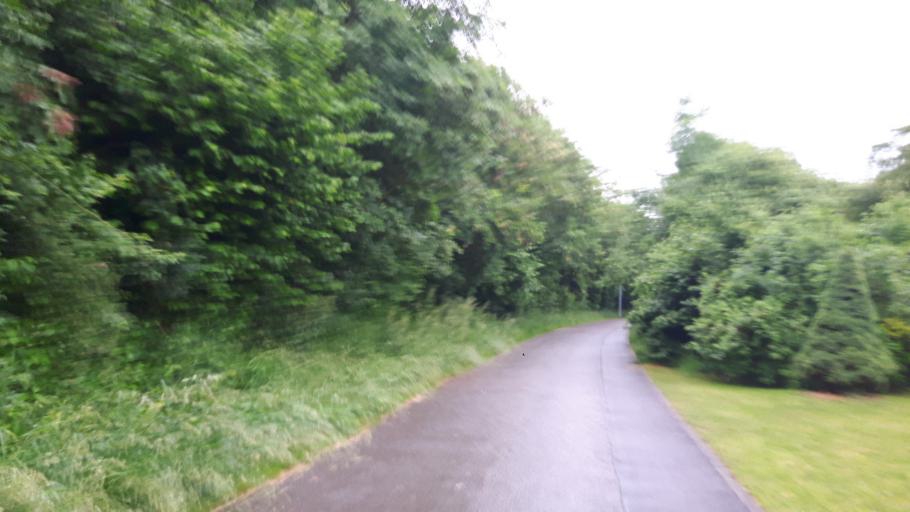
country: DE
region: Bavaria
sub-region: Regierungsbezirk Unterfranken
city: Schweinfurt
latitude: 50.0591
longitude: 10.2314
